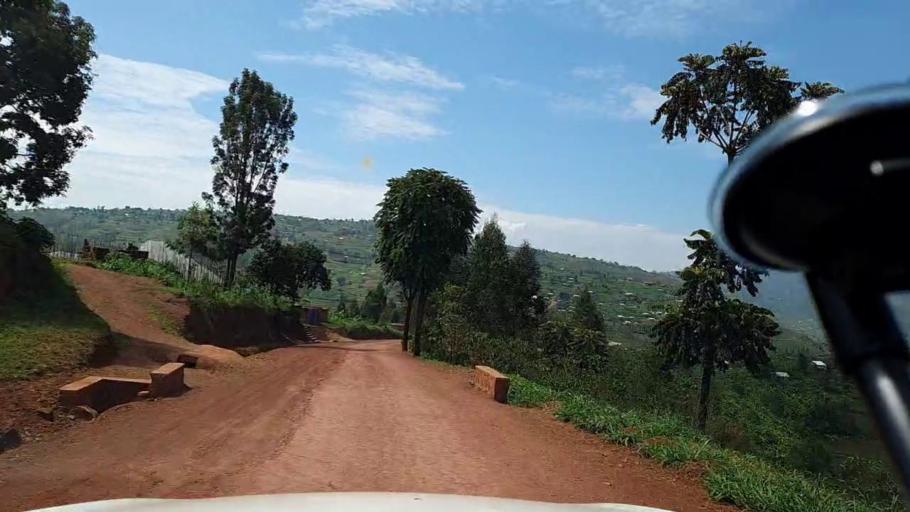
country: RW
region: Kigali
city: Kigali
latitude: -1.7977
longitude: 29.8974
